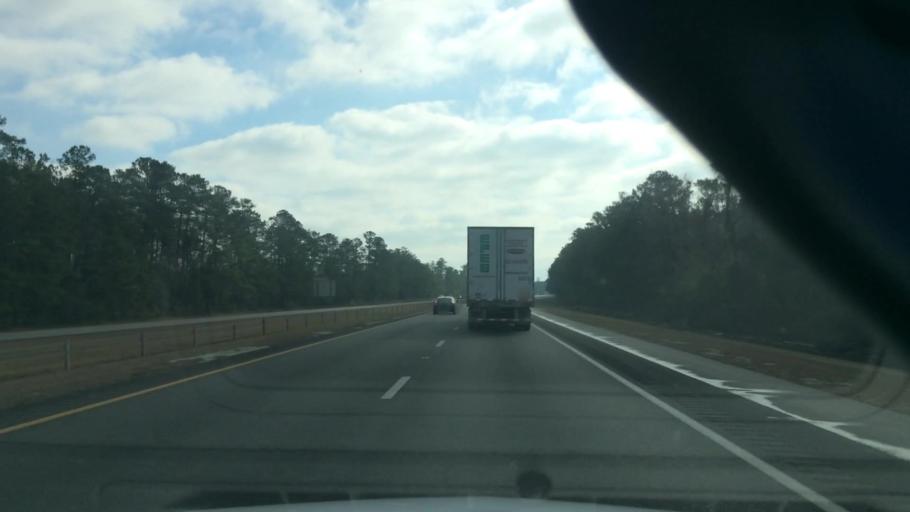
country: US
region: North Carolina
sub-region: Pender County
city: Burgaw
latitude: 34.5586
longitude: -77.8953
